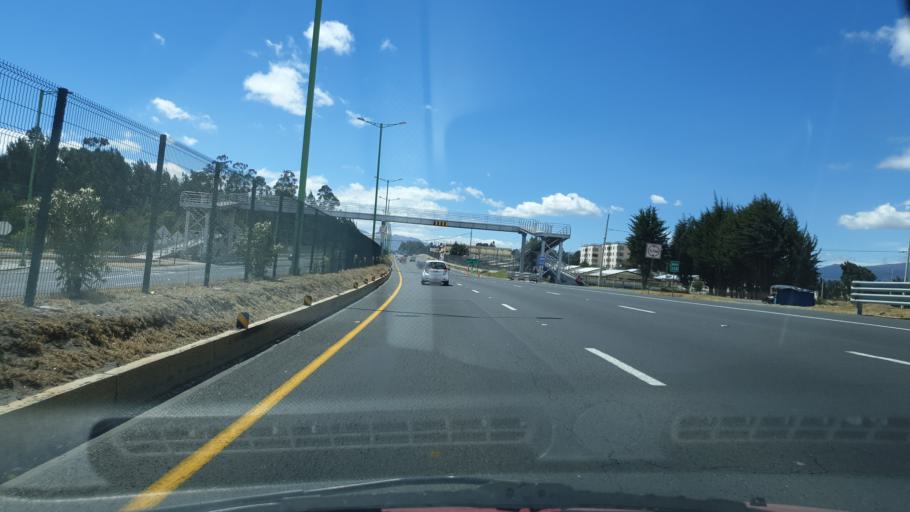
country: EC
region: Cotopaxi
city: Saquisili
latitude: -0.8522
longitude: -78.6196
